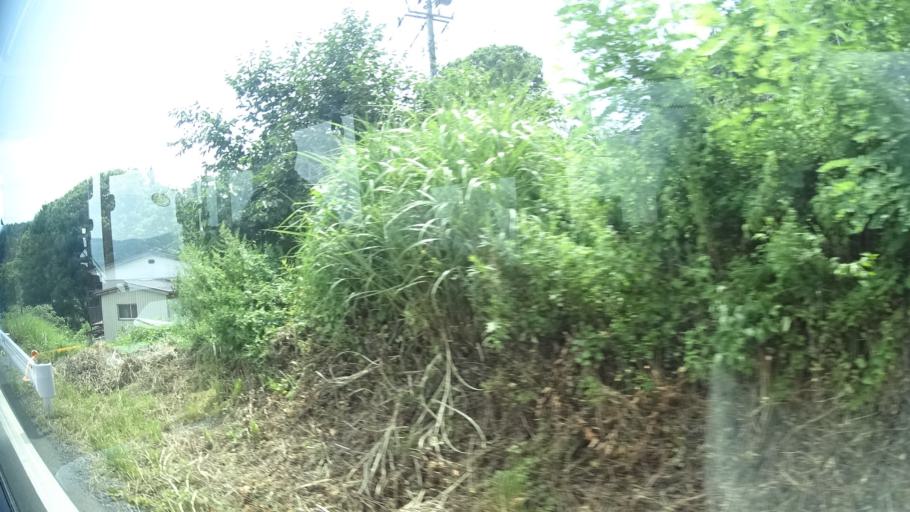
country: JP
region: Miyagi
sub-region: Oshika Gun
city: Onagawa Cho
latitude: 38.6652
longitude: 141.4446
